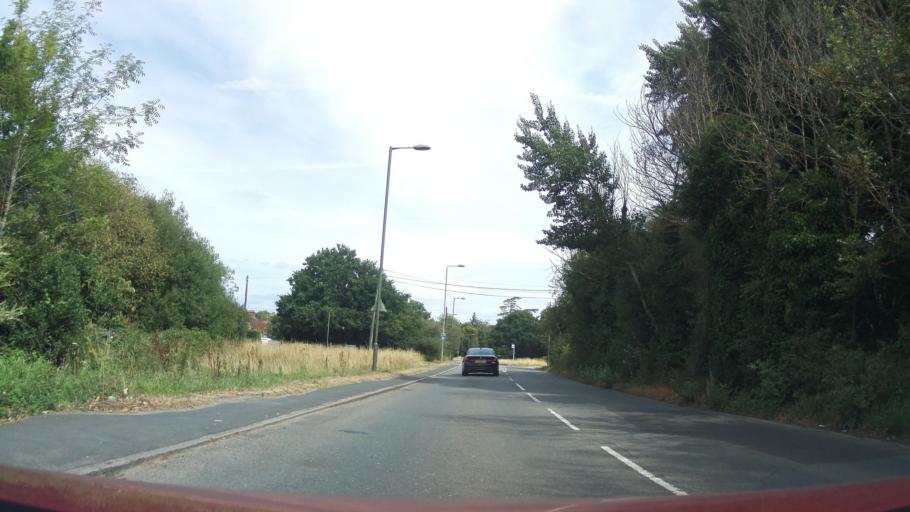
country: GB
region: England
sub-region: Surrey
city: Reigate
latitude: 51.2156
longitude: -0.2021
